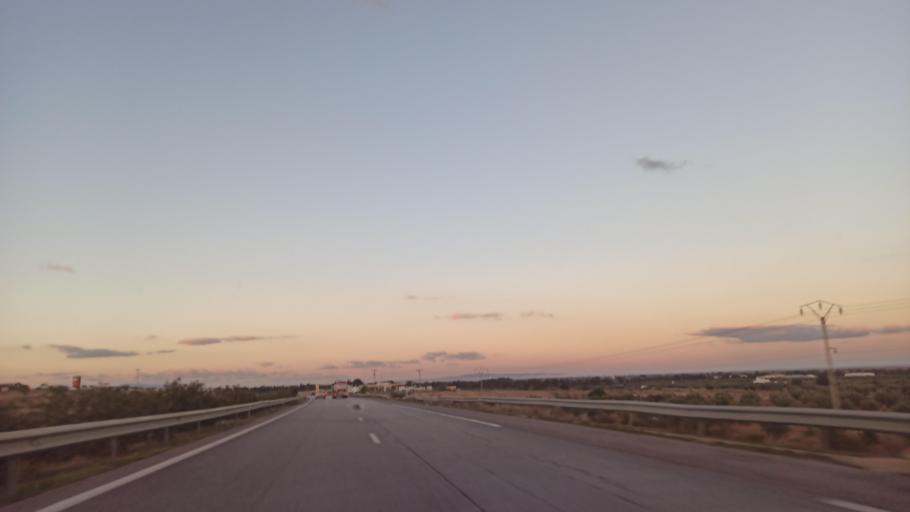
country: TN
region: Susah
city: Harqalah
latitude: 36.2432
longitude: 10.4229
